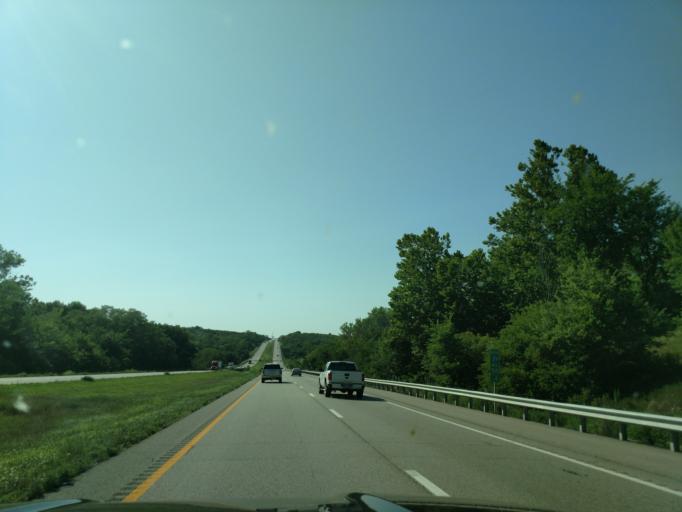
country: US
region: Missouri
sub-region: Andrew County
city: Savannah
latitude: 39.9001
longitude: -94.8787
